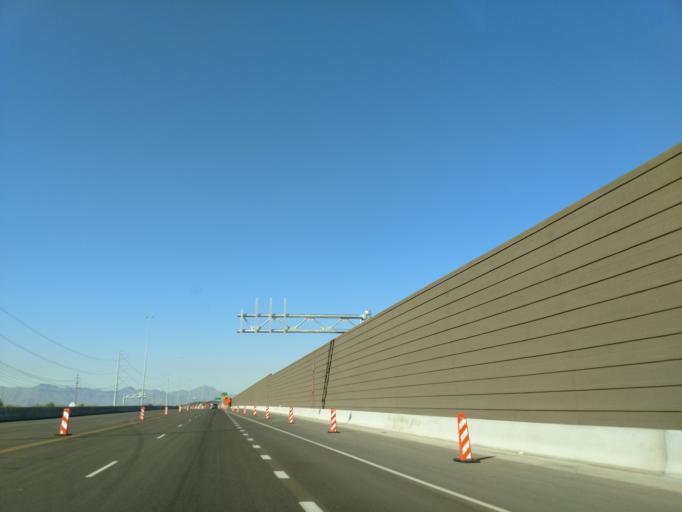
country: US
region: Arizona
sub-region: Maricopa County
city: Guadalupe
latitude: 33.2920
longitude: -112.0041
